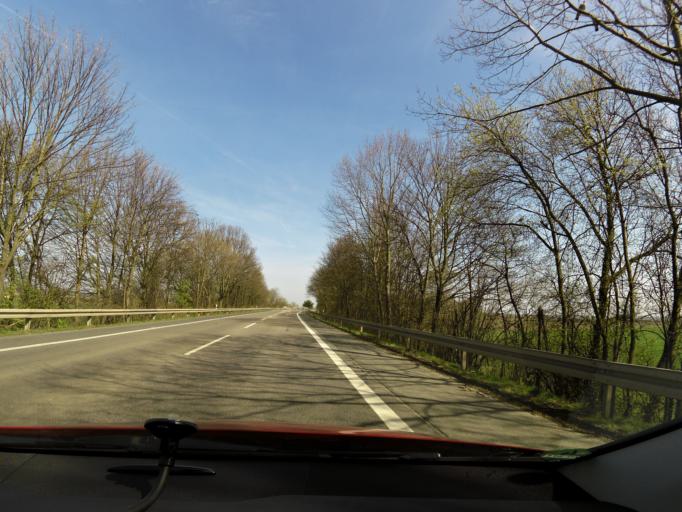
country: DE
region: North Rhine-Westphalia
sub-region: Regierungsbezirk Koln
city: Rheinbach
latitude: 50.6254
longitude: 6.9826
